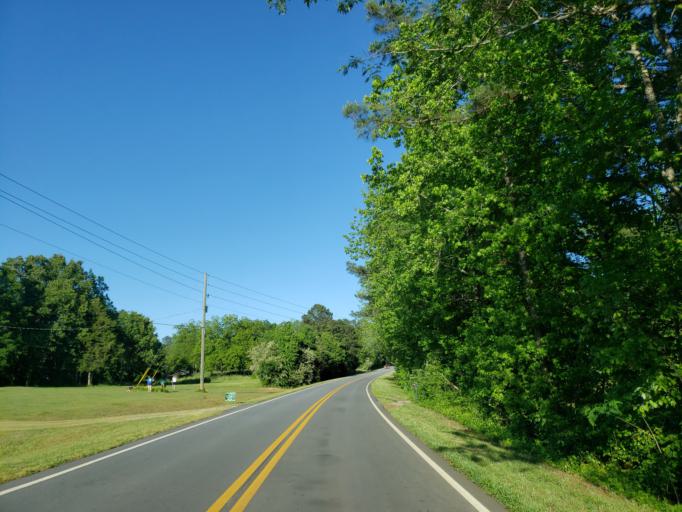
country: US
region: Georgia
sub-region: Haralson County
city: Buchanan
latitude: 33.8102
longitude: -85.2298
